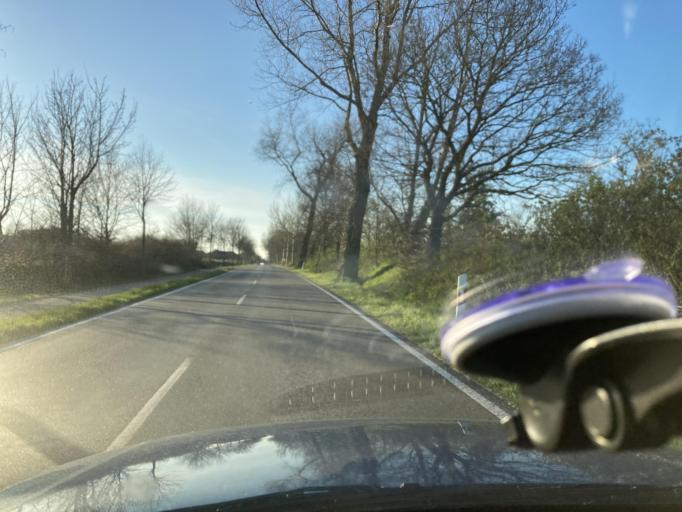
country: DE
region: Schleswig-Holstein
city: Weddingstedt
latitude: 54.2319
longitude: 9.0978
